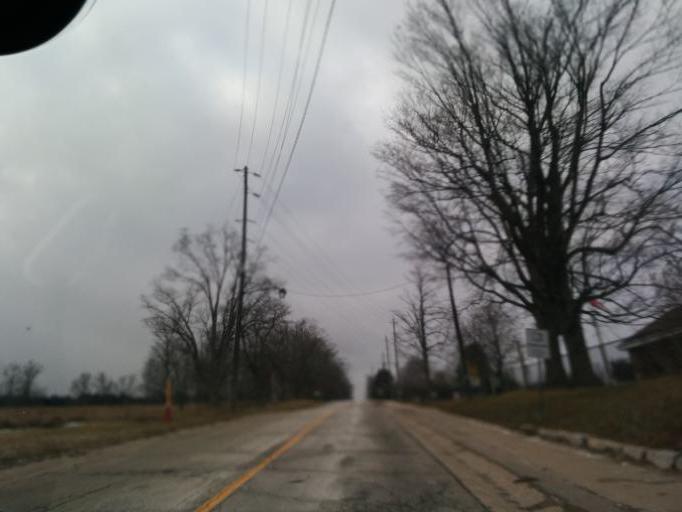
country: CA
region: Ontario
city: Orangeville
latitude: 43.7991
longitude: -79.9370
